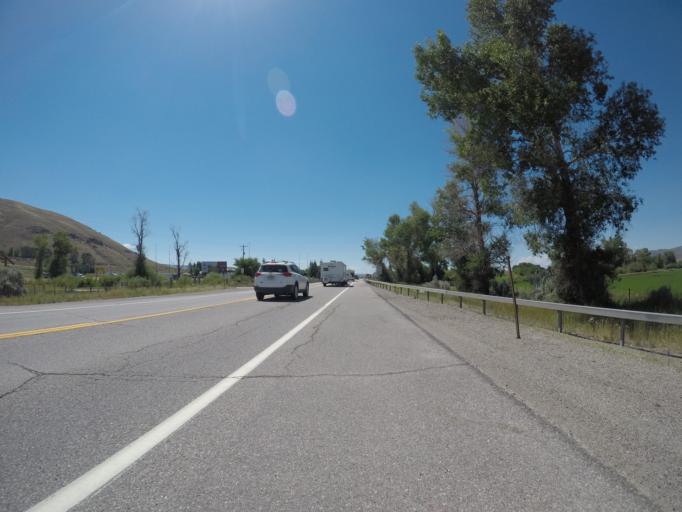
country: US
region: Idaho
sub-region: Bear Lake County
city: Montpelier
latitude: 42.0889
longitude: -110.9494
